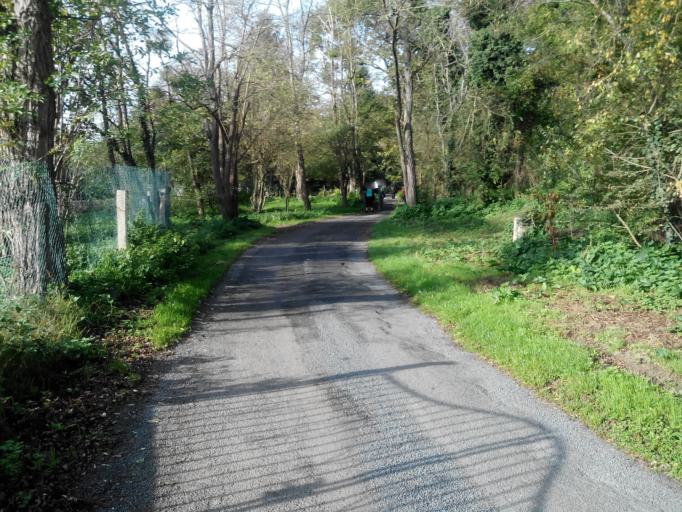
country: FR
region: Centre
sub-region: Departement d'Indre-et-Loire
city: Fondettes
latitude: 47.3852
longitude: 0.6273
